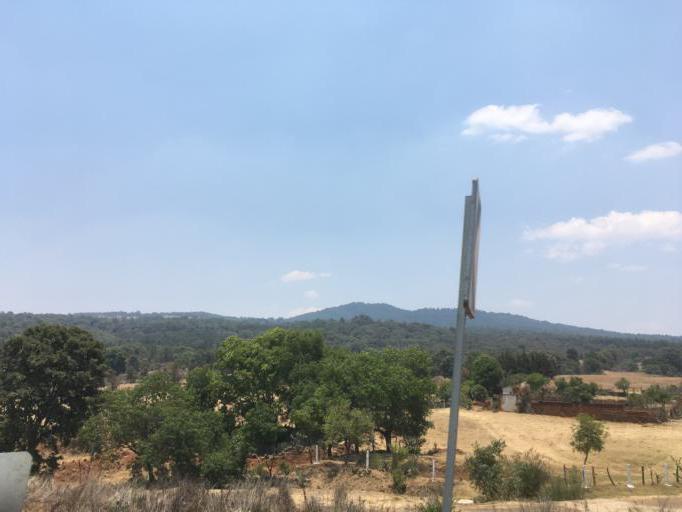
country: MX
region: Michoacan
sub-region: Morelia
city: Iratzio
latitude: 19.6343
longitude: -101.4697
